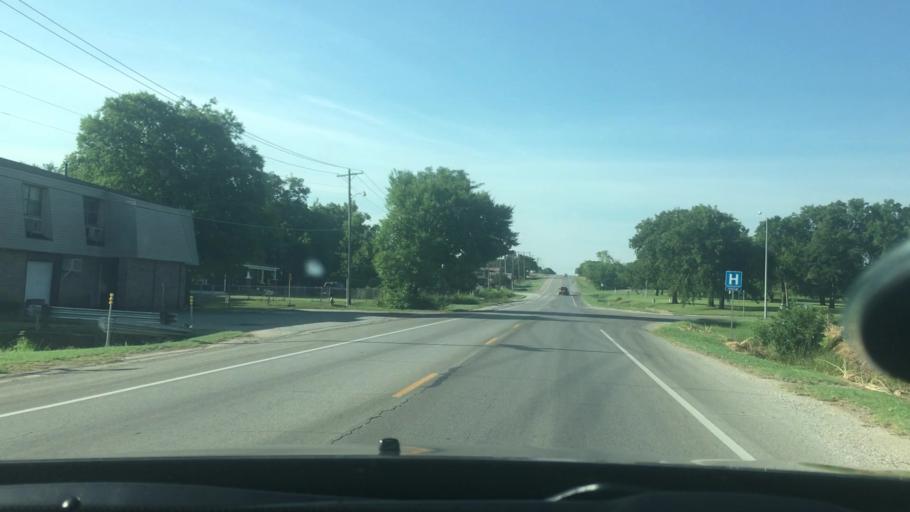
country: US
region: Oklahoma
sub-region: Garvin County
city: Pauls Valley
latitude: 34.7209
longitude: -97.2130
